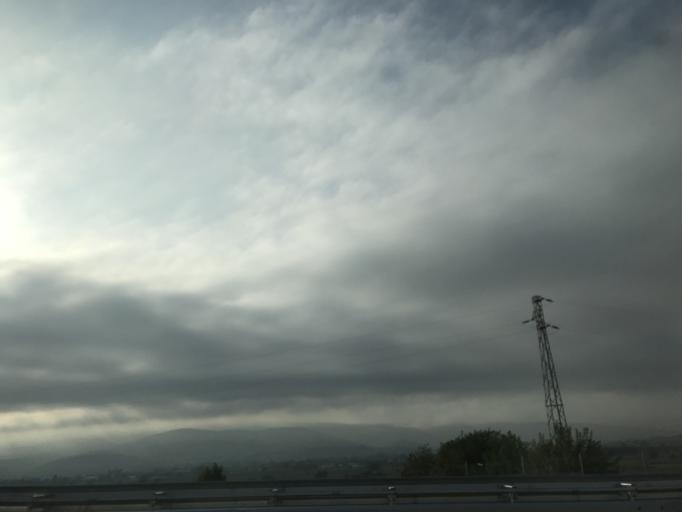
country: TR
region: Balikesir
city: Susurluk
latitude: 39.9373
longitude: 28.1428
